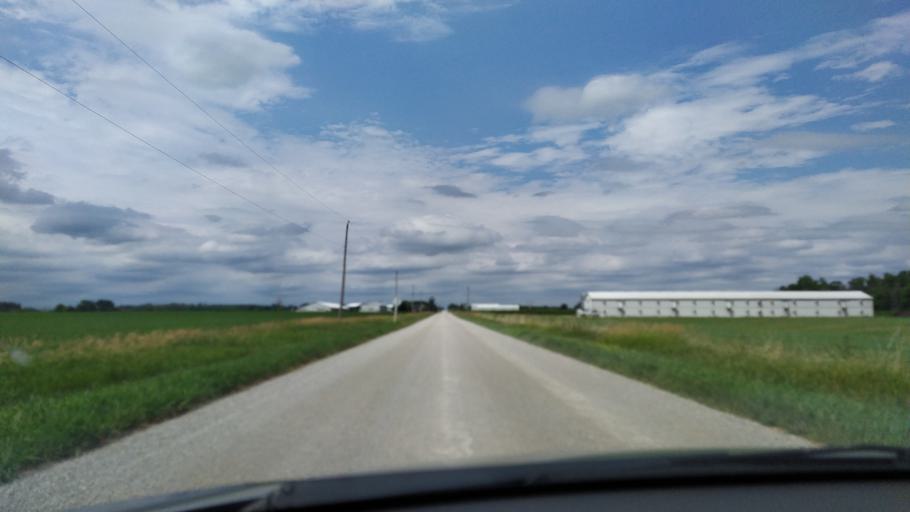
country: CA
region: Ontario
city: Stratford
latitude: 43.3545
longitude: -80.9126
